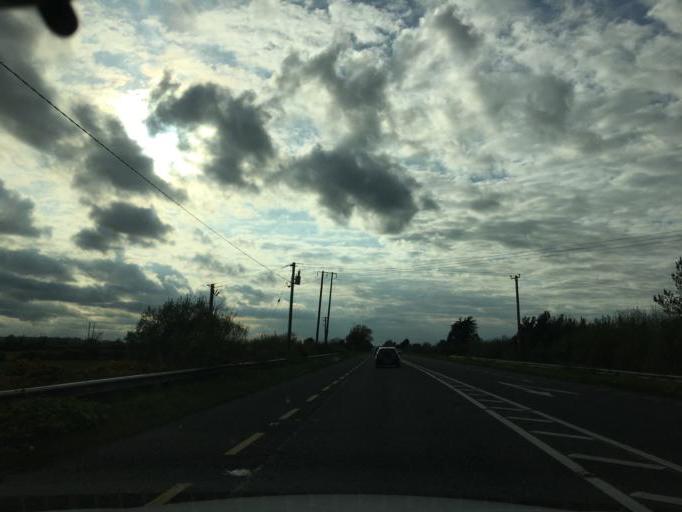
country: IE
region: Leinster
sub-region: Loch Garman
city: Loch Garman
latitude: 52.3427
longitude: -6.5805
